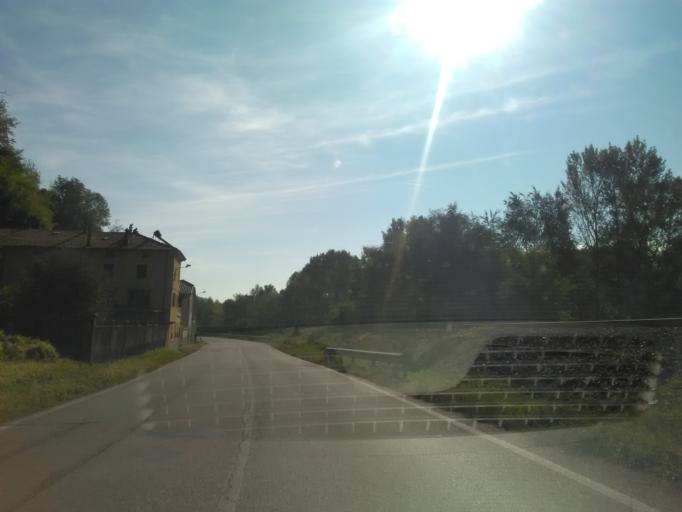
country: IT
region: Piedmont
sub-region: Provincia di Vercelli
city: Serravalle Sesia
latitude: 45.6988
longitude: 8.3076
